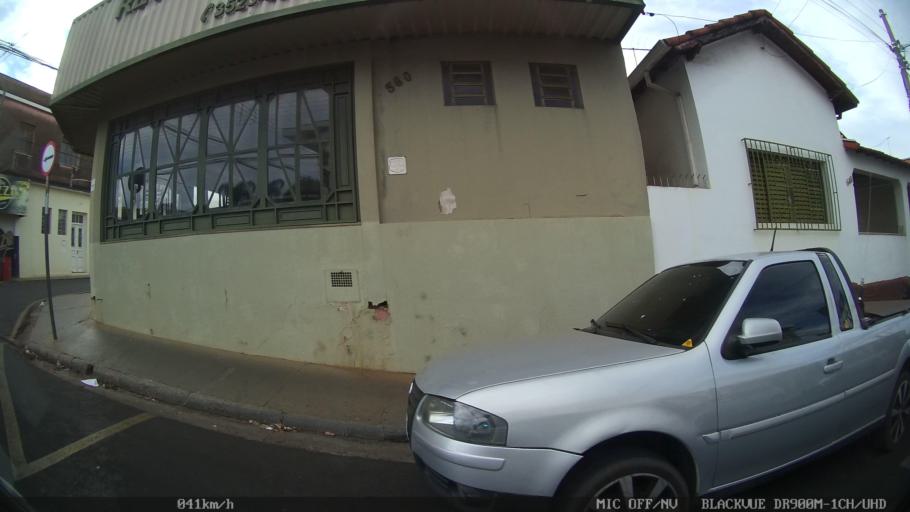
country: BR
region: Sao Paulo
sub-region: Catanduva
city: Catanduva
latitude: -21.1264
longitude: -48.9678
